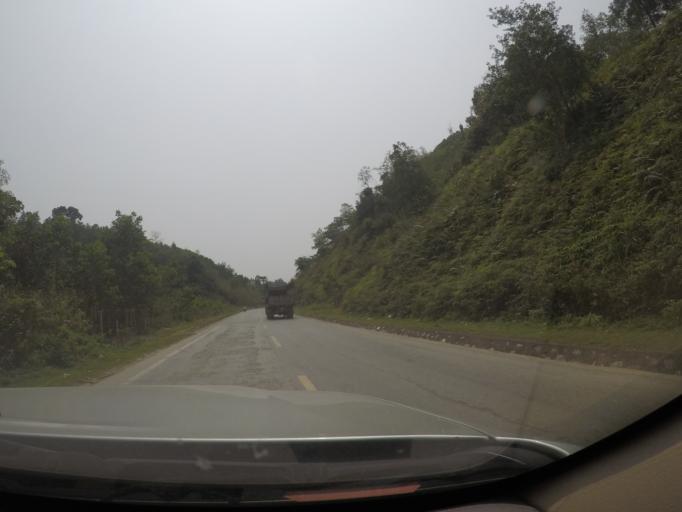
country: VN
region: Thanh Hoa
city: Thi Tran Yen Cat
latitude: 19.6714
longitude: 105.4536
